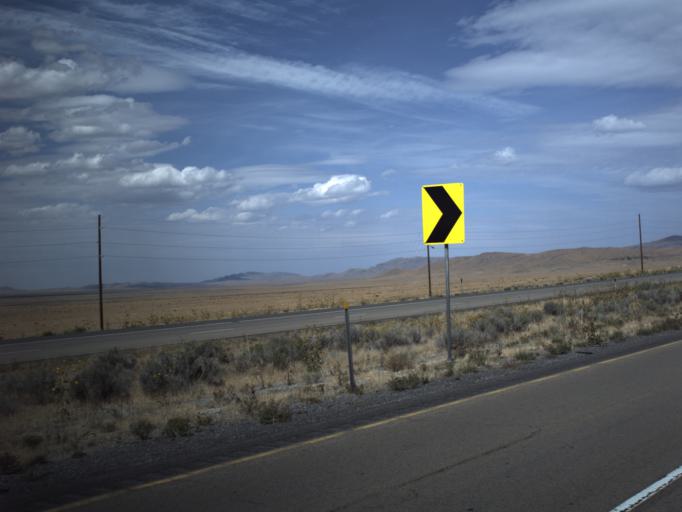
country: US
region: Utah
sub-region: Tooele County
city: Grantsville
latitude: 40.8090
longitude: -112.9313
